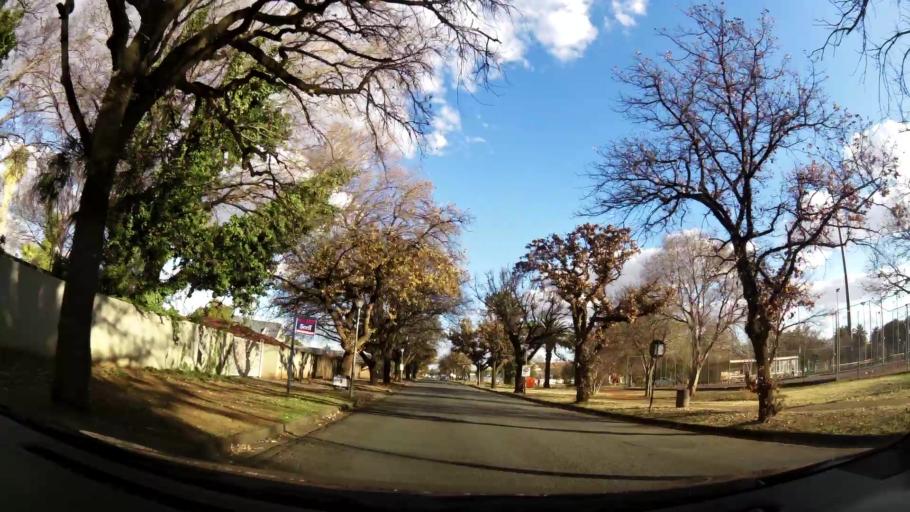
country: ZA
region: North-West
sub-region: Dr Kenneth Kaunda District Municipality
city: Potchefstroom
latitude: -26.7116
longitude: 27.0912
